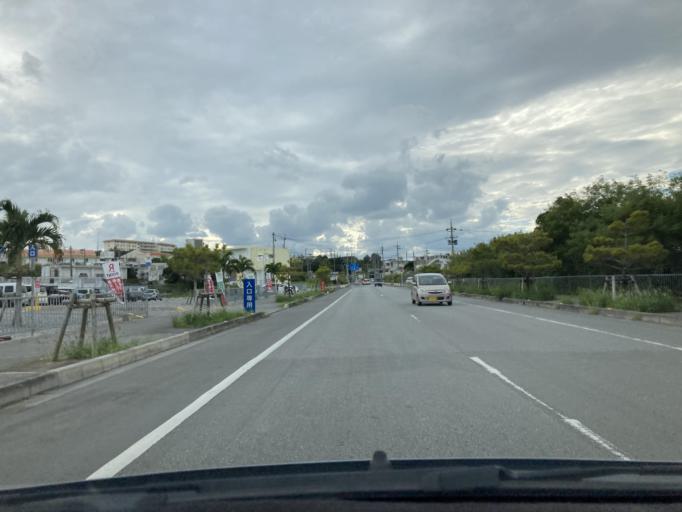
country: JP
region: Okinawa
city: Katsuren-haebaru
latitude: 26.3306
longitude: 127.8862
